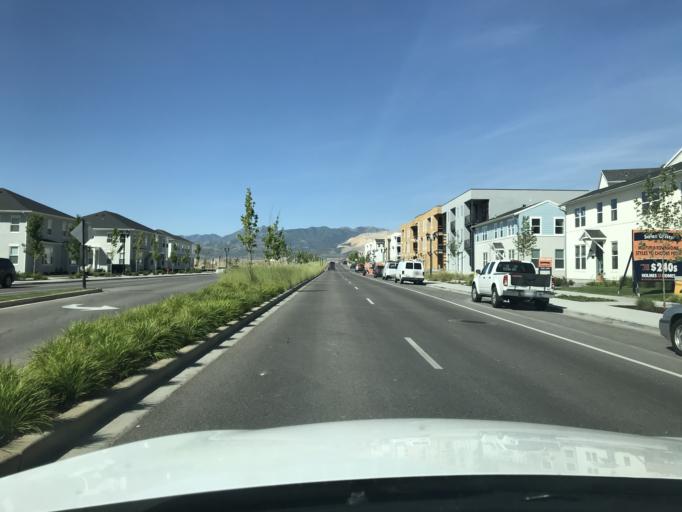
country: US
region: Utah
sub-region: Salt Lake County
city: Herriman
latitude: 40.5595
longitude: -112.0151
